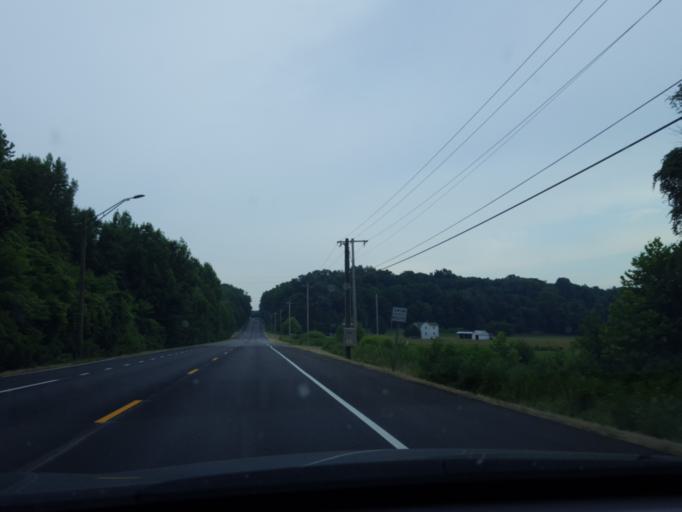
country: US
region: Maryland
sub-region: Charles County
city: La Plata
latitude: 38.4157
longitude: -76.9017
